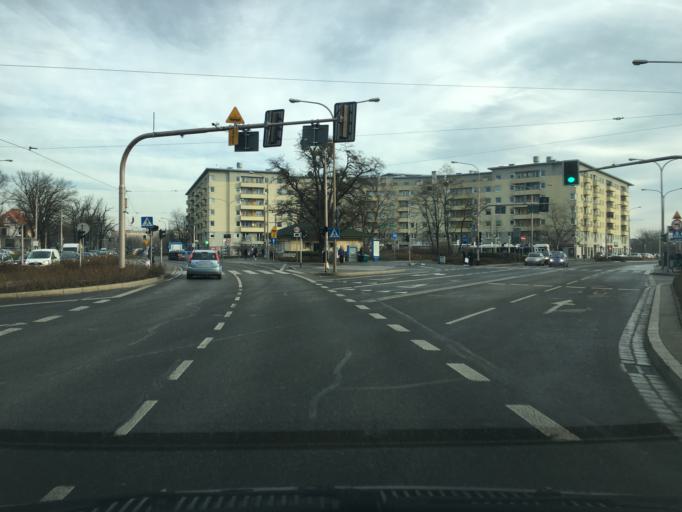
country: PL
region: Lower Silesian Voivodeship
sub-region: Powiat wroclawski
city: Wroclaw
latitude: 51.1318
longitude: 17.0641
